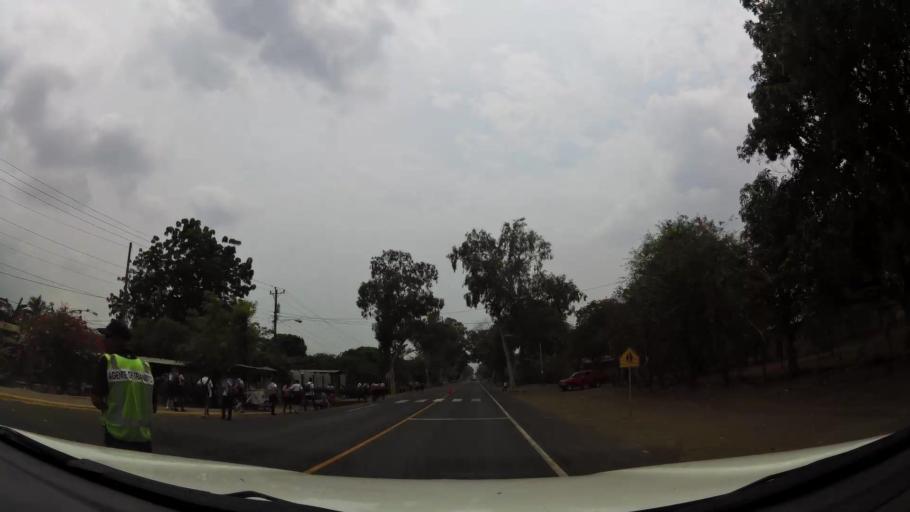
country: NI
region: Leon
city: Quezalguaque
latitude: 12.5356
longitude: -86.9017
